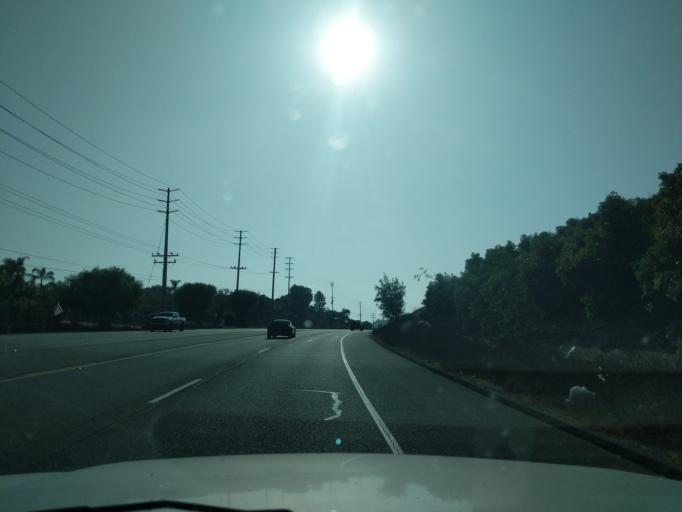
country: US
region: California
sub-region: Ventura County
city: Moorpark
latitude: 34.2687
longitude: -118.8364
